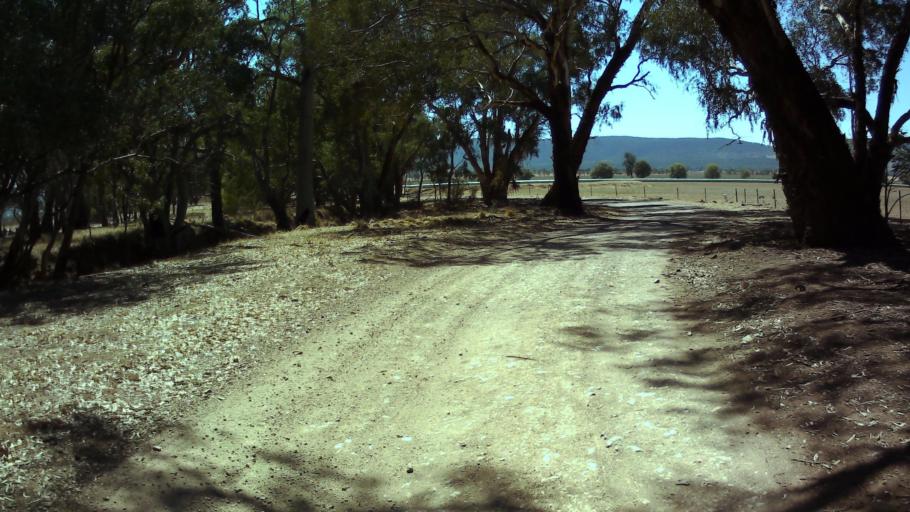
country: AU
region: New South Wales
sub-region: Weddin
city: Grenfell
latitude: -33.6998
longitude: 148.3041
